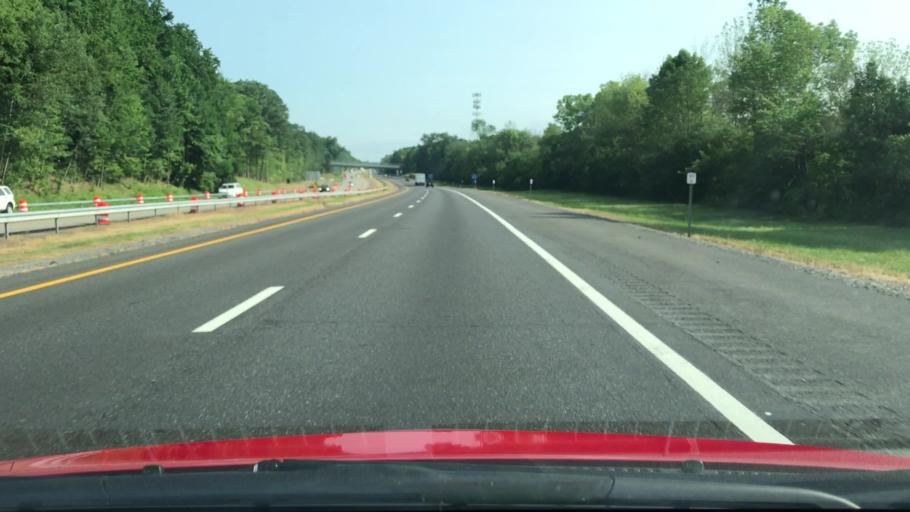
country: US
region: New York
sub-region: Orange County
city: Gardnertown
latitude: 41.5170
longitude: -74.0735
